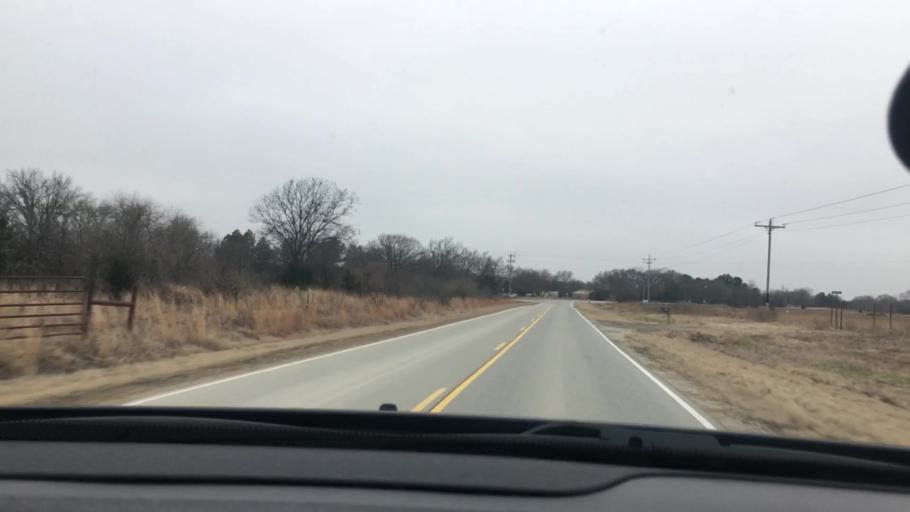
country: US
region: Oklahoma
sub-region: Coal County
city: Coalgate
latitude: 34.5070
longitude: -96.3004
